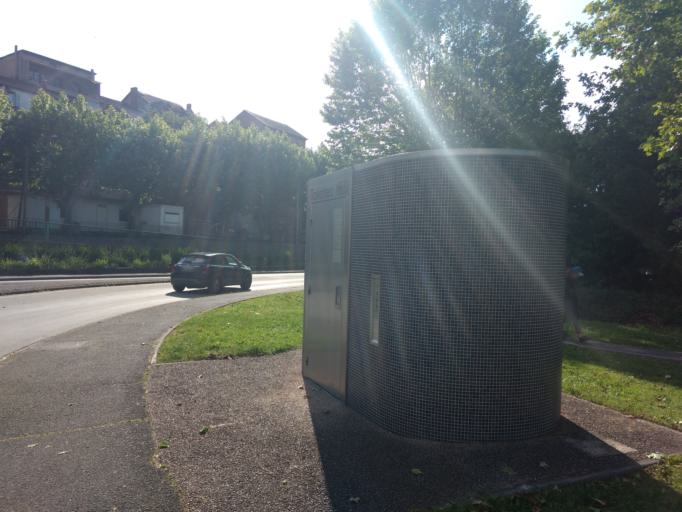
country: FR
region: Midi-Pyrenees
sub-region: Departement de l'Aveyron
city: Decazeville
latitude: 44.5584
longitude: 2.2558
